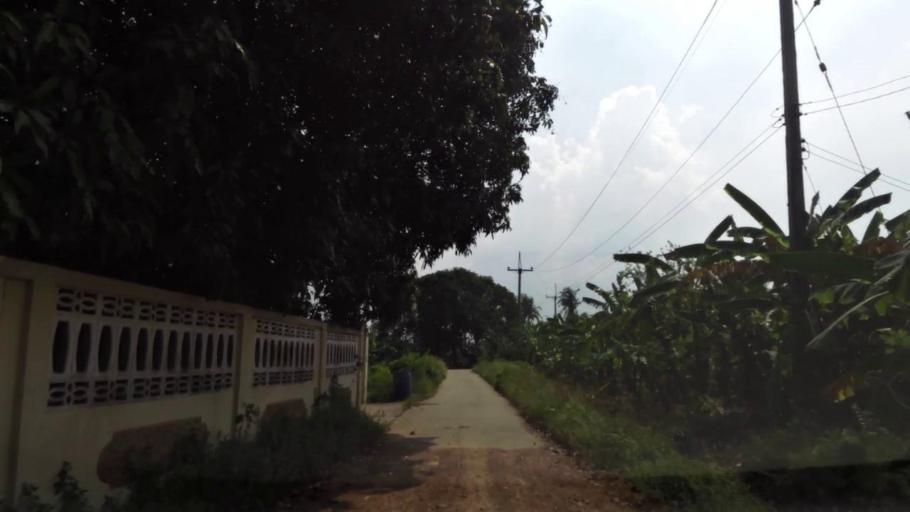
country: TH
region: Ang Thong
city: Pho Thong
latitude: 14.6220
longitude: 100.3969
